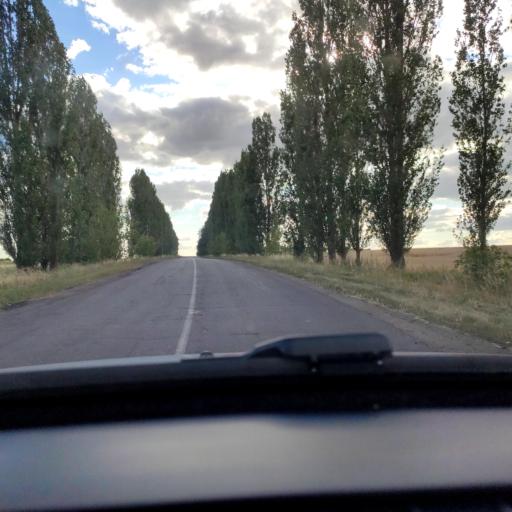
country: RU
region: Voronezj
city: Orlovo
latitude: 51.6161
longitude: 39.8050
